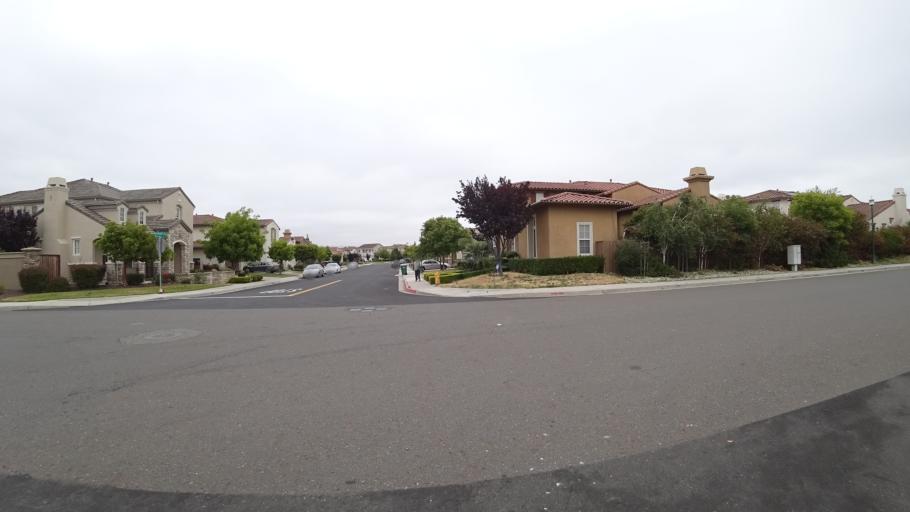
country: US
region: California
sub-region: Alameda County
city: Hayward
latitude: 37.6076
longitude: -122.0947
